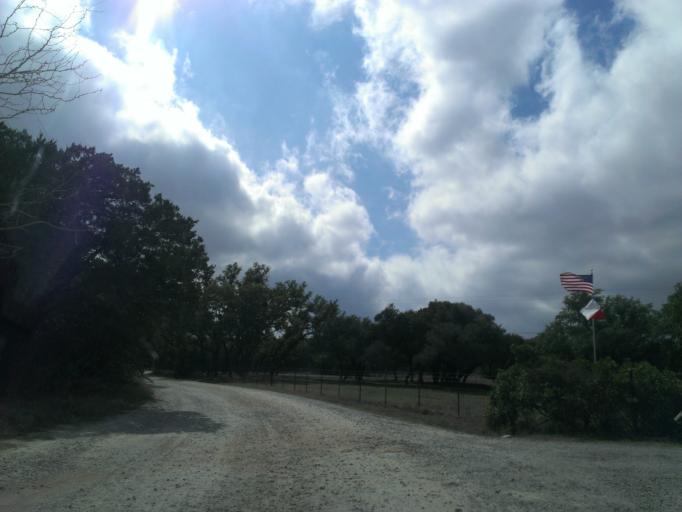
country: US
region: Texas
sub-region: Travis County
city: Briarcliff
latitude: 30.3829
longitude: -98.0956
